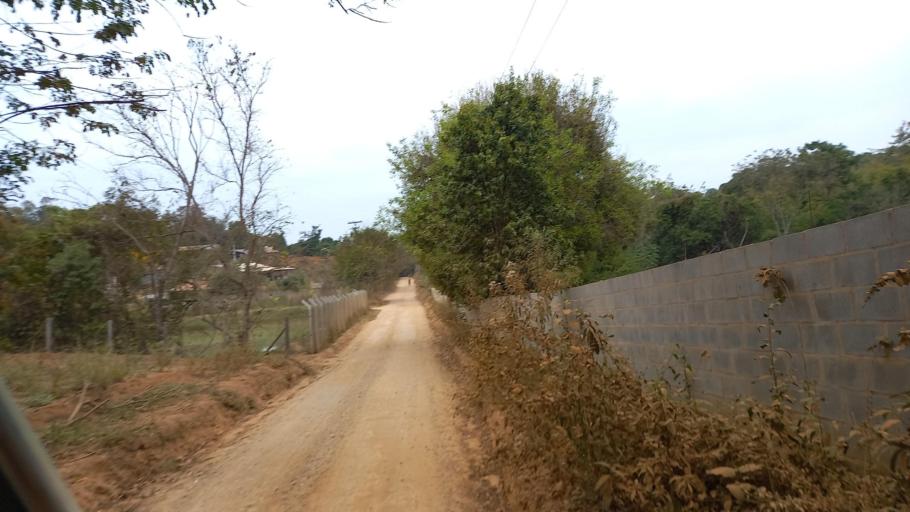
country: BR
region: Sao Paulo
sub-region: Moji-Guacu
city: Mogi-Gaucu
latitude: -22.2961
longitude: -46.8321
